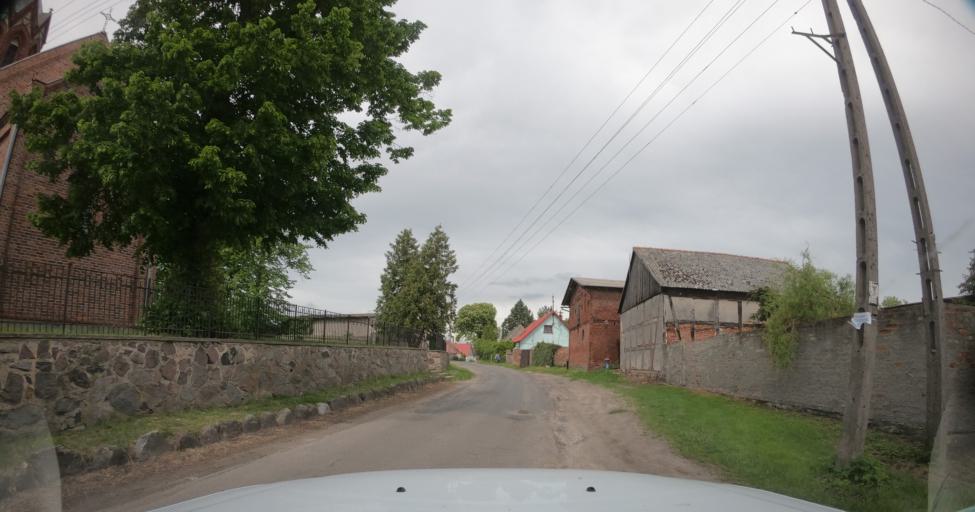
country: PL
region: West Pomeranian Voivodeship
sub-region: Powiat pyrzycki
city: Kozielice
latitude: 53.0767
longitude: 14.8797
